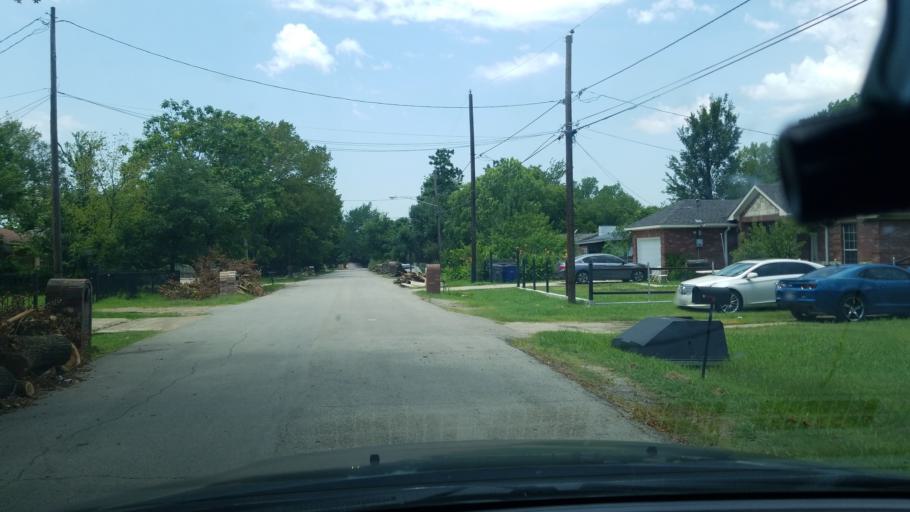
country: US
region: Texas
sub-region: Dallas County
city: Balch Springs
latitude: 32.7159
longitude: -96.6511
